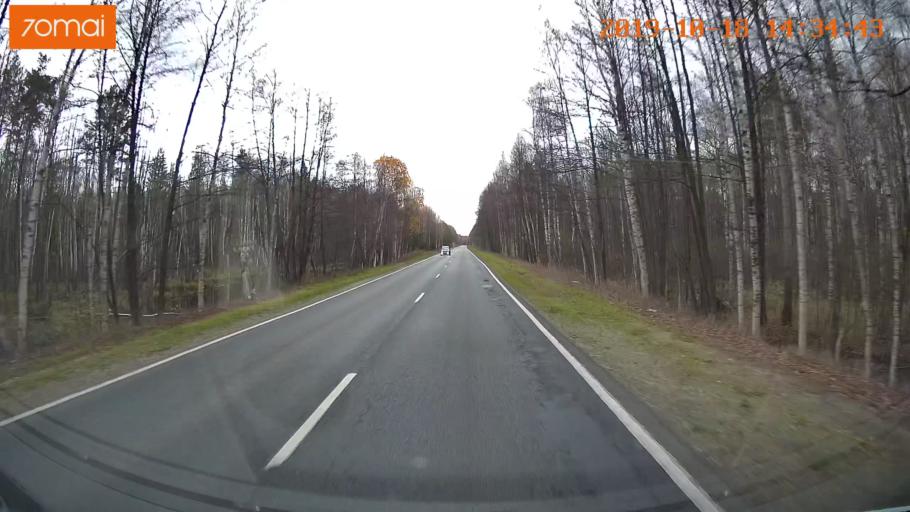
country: RU
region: Vladimir
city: Velikodvorskiy
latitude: 55.2152
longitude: 40.6216
